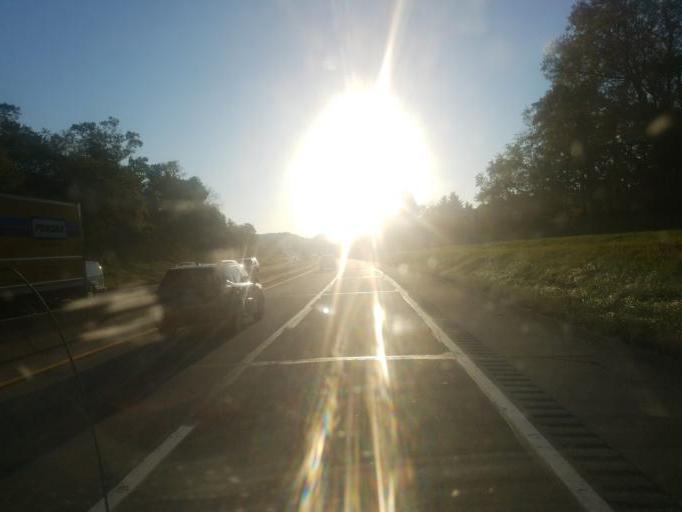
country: US
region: Pennsylvania
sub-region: Allegheny County
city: Bradford Woods
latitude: 40.6566
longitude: -80.0809
